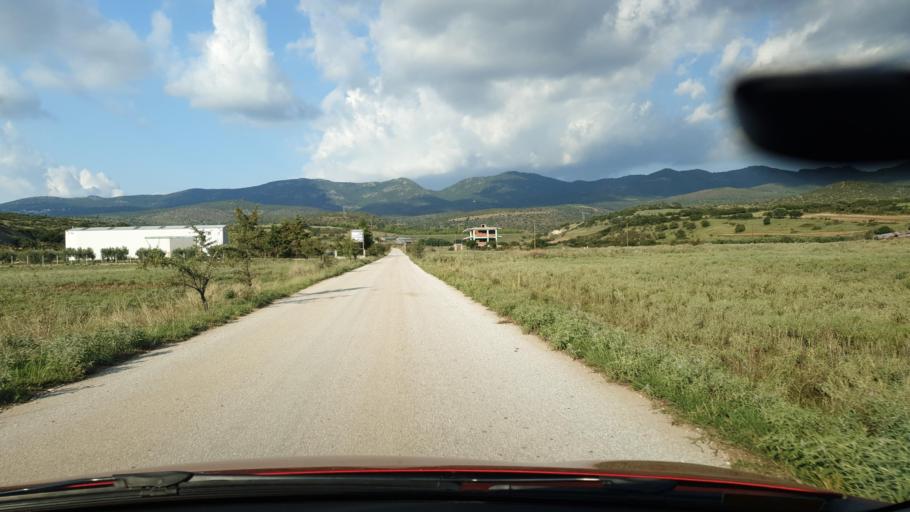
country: GR
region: Central Macedonia
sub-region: Nomos Thessalonikis
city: Vasilika
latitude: 40.5003
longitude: 23.1443
